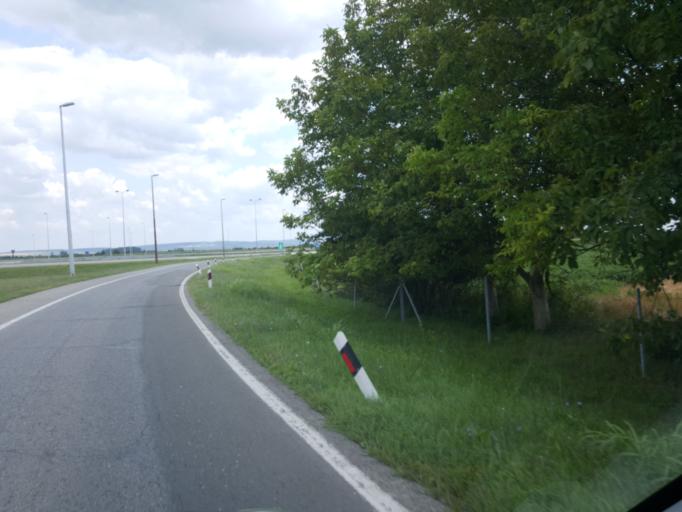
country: RS
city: Ravnje
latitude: 45.0388
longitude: 19.3874
